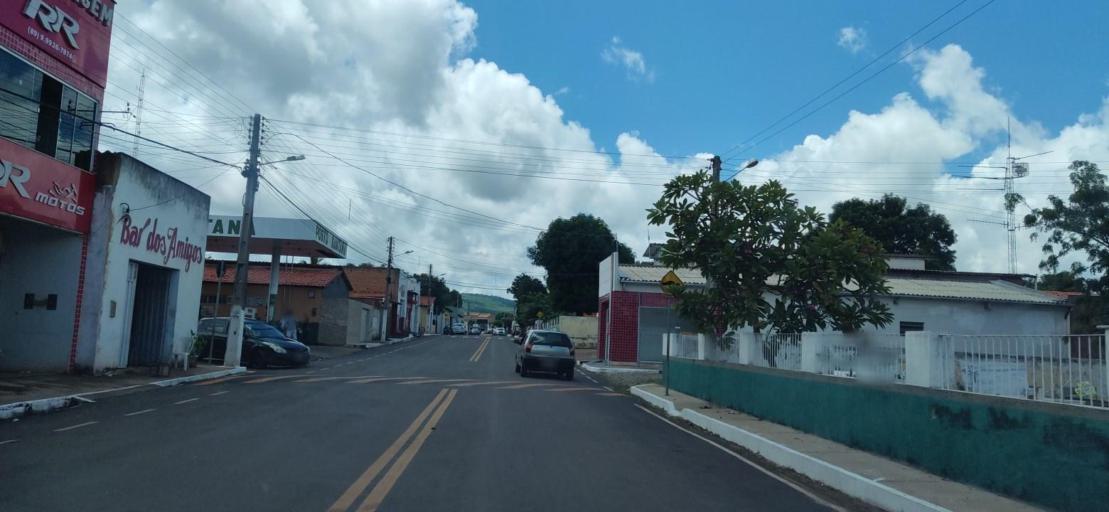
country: BR
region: Piaui
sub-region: Valenca Do Piaui
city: Valenca do Piaui
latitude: -6.1111
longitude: -41.7901
